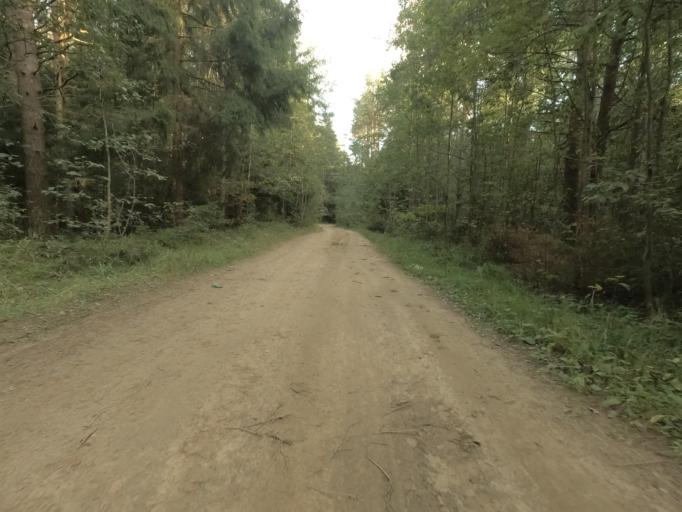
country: RU
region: Leningrad
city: Otradnoye
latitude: 59.8523
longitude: 30.7959
